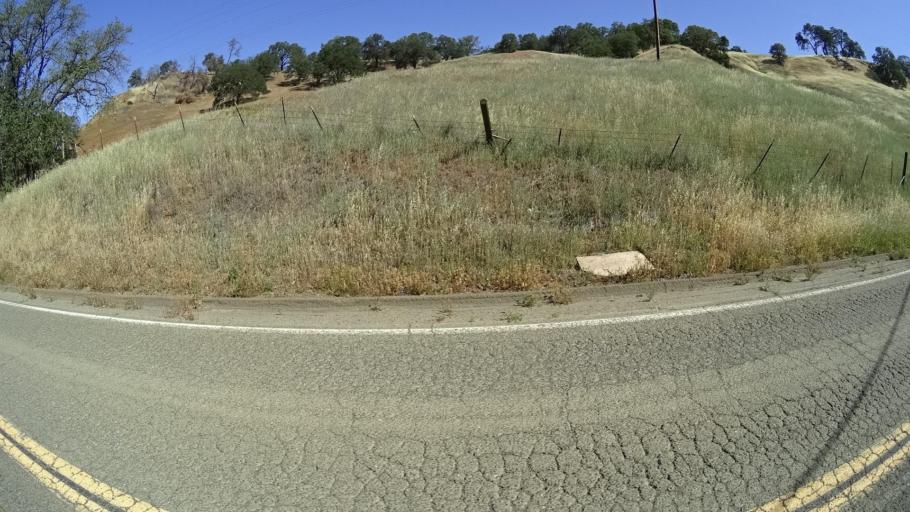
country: US
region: California
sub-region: Lake County
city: Lower Lake
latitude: 38.8989
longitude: -122.5622
